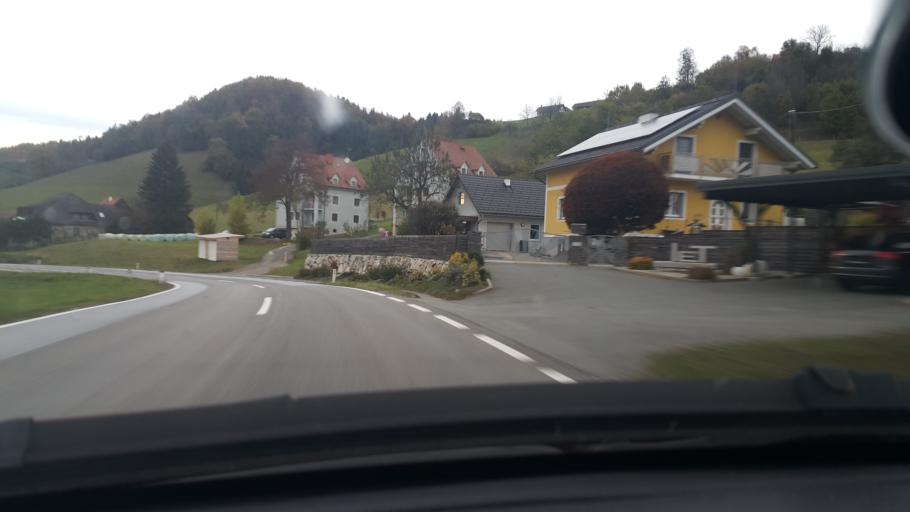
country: AT
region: Styria
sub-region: Politischer Bezirk Leibnitz
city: Arnfels
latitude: 46.6705
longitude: 15.4342
